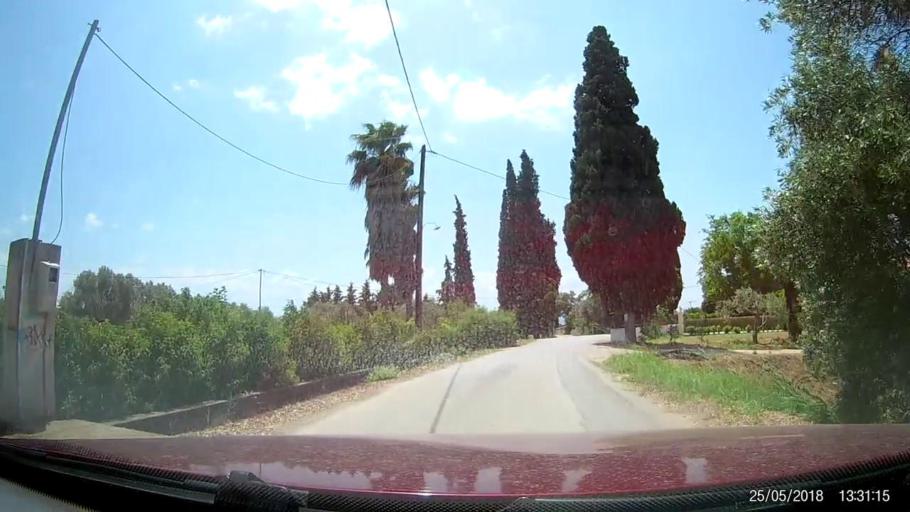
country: GR
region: Central Greece
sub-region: Nomos Evvoias
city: Mytikas
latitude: 38.4377
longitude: 23.6574
